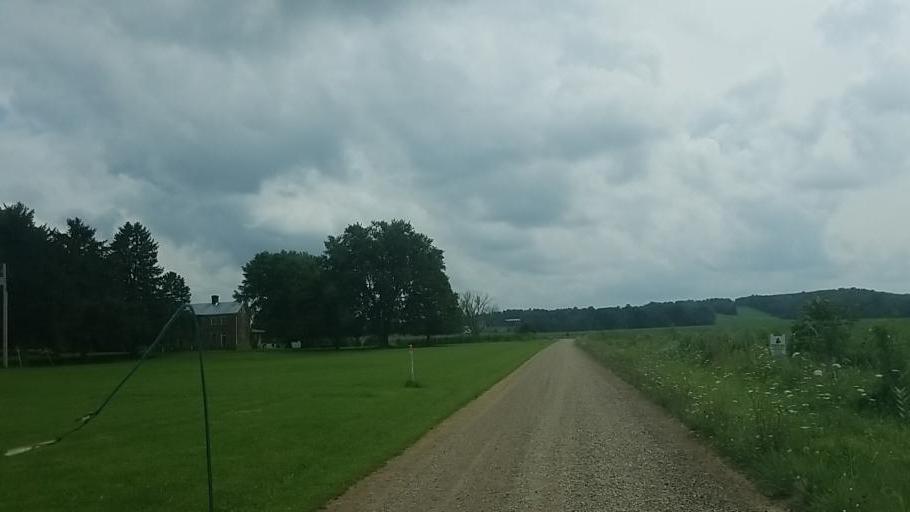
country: US
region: Ohio
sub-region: Knox County
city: Gambier
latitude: 40.3152
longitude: -82.3759
